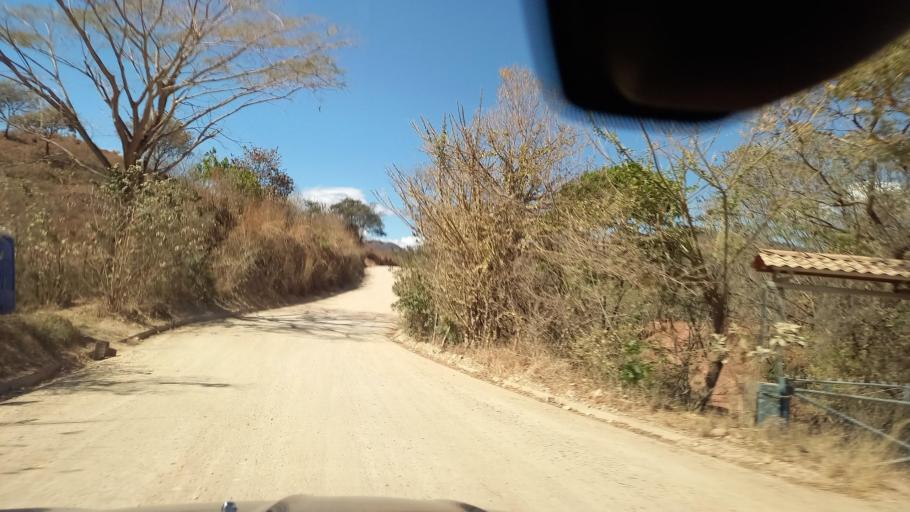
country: SV
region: Santa Ana
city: Metapan
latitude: 14.3621
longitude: -89.4568
